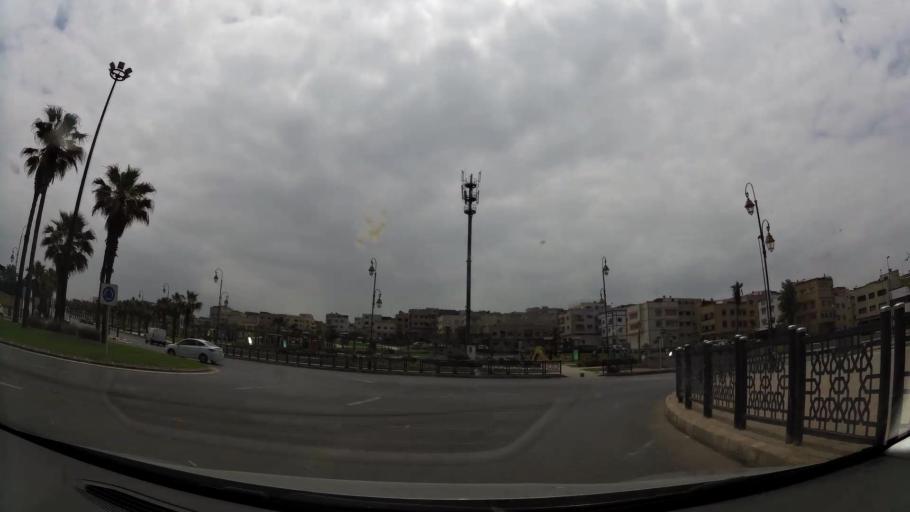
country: MA
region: Rabat-Sale-Zemmour-Zaer
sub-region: Rabat
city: Rabat
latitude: 33.9904
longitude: -6.8828
